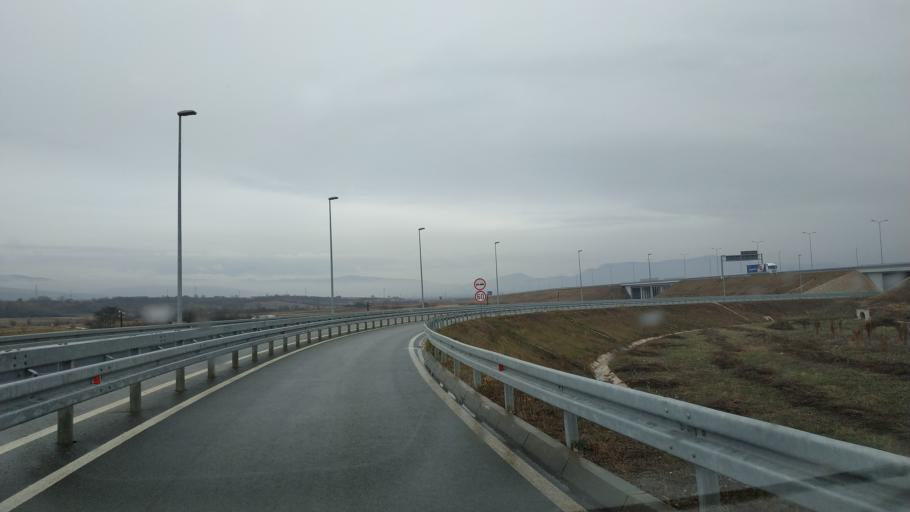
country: RS
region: Central Serbia
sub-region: Pirotski Okrug
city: Pirot
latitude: 43.1188
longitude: 22.6205
